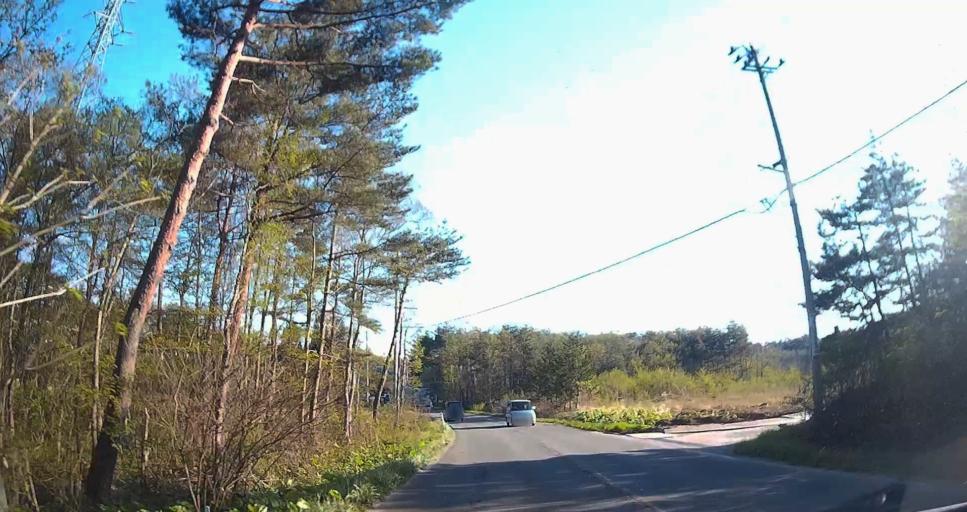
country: JP
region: Aomori
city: Mutsu
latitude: 41.3398
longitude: 141.2144
